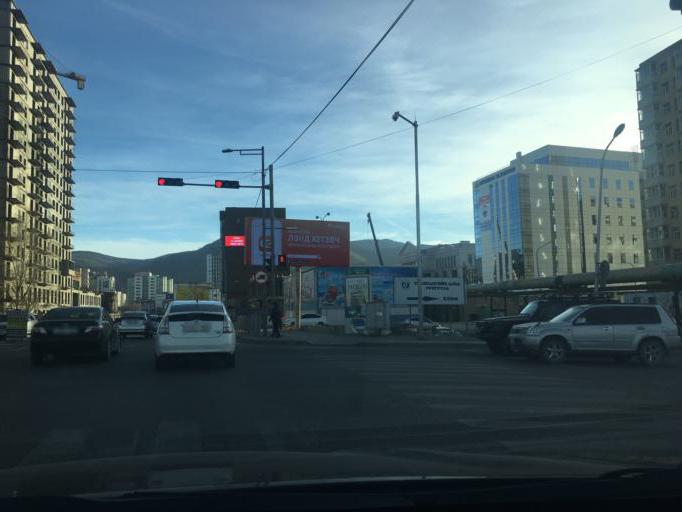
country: MN
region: Ulaanbaatar
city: Ulaanbaatar
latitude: 47.9019
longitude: 106.8931
